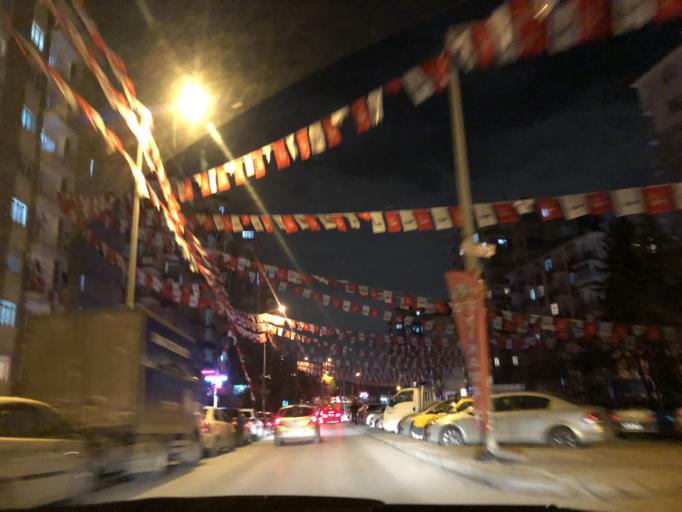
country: TR
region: Ankara
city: Batikent
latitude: 39.9653
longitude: 32.7947
